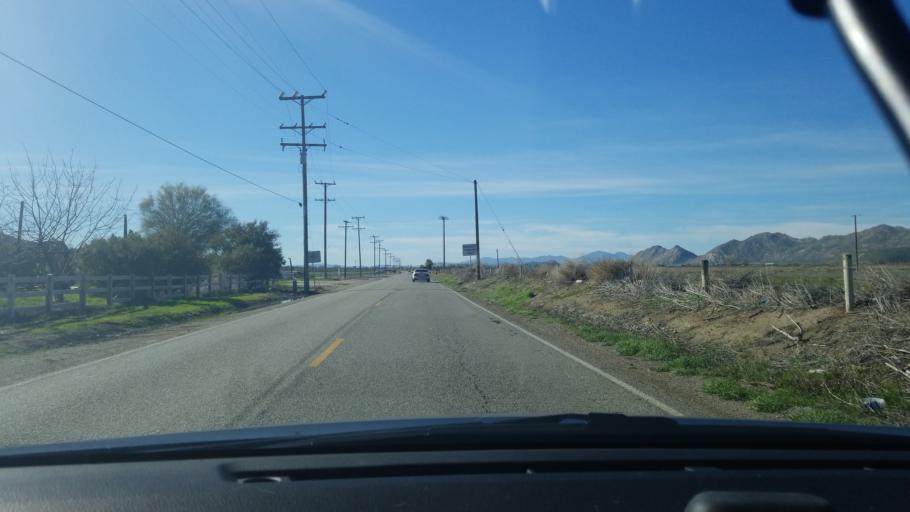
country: US
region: California
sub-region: Riverside County
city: Lakeview
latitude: 33.8593
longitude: -117.0618
